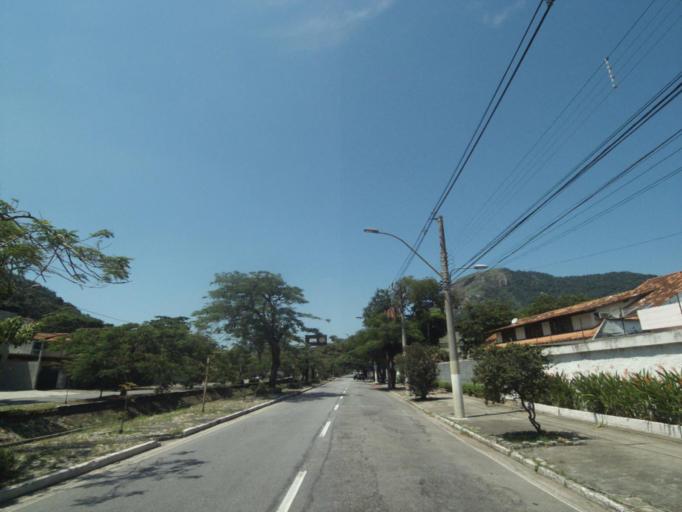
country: BR
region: Rio de Janeiro
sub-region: Niteroi
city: Niteroi
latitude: -22.9144
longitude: -43.0892
